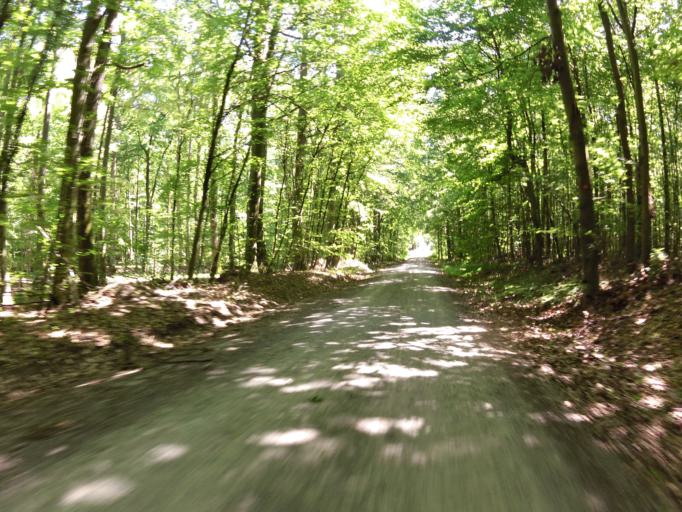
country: DE
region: Bavaria
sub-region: Regierungsbezirk Unterfranken
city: Kleinrinderfeld
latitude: 49.7034
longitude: 9.8672
